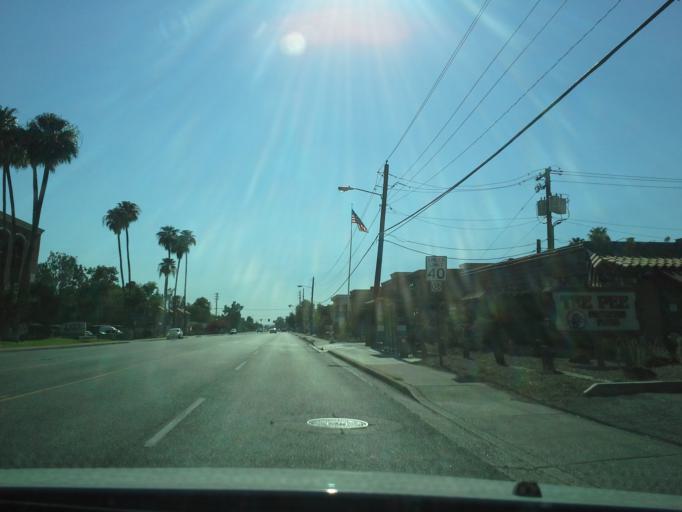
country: US
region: Arizona
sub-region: Maricopa County
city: Paradise Valley
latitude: 33.4951
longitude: -111.9913
